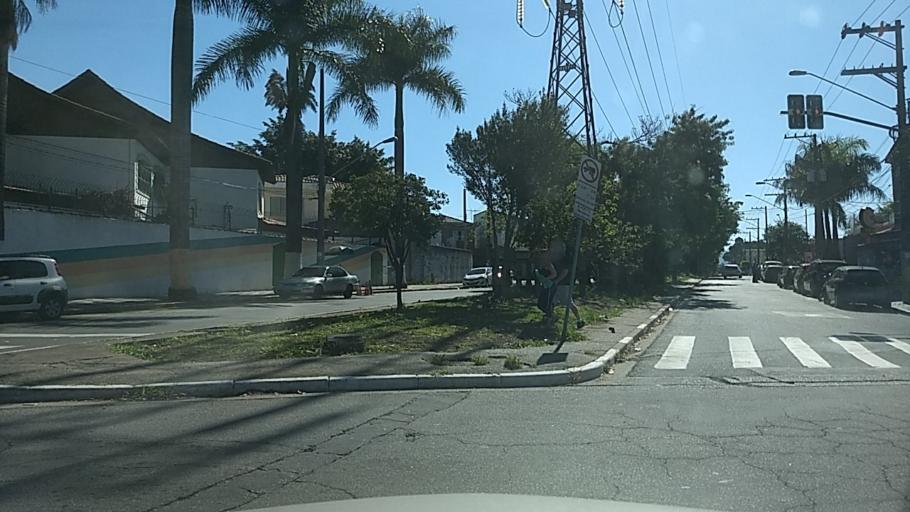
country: BR
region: Sao Paulo
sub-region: Guarulhos
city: Guarulhos
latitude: -23.4960
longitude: -46.5722
